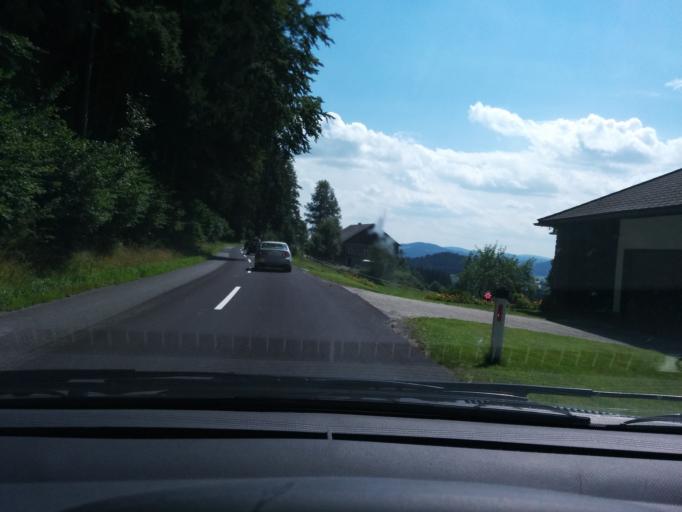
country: AT
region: Upper Austria
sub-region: Politischer Bezirk Rohrbach
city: Ulrichsberg
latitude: 48.7161
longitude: 13.8991
